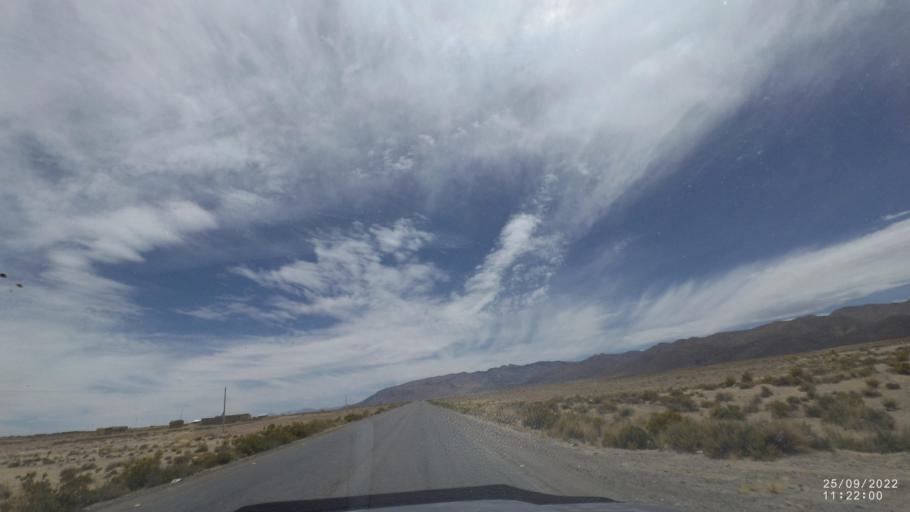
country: BO
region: Oruro
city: Challapata
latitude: -19.1335
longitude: -66.7691
